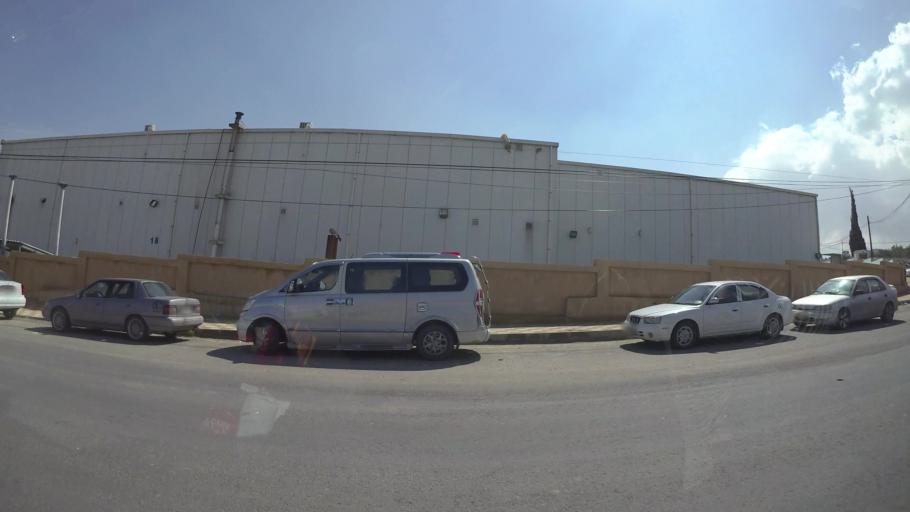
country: JO
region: Zarqa
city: Russeifa
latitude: 31.9945
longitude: 36.0070
